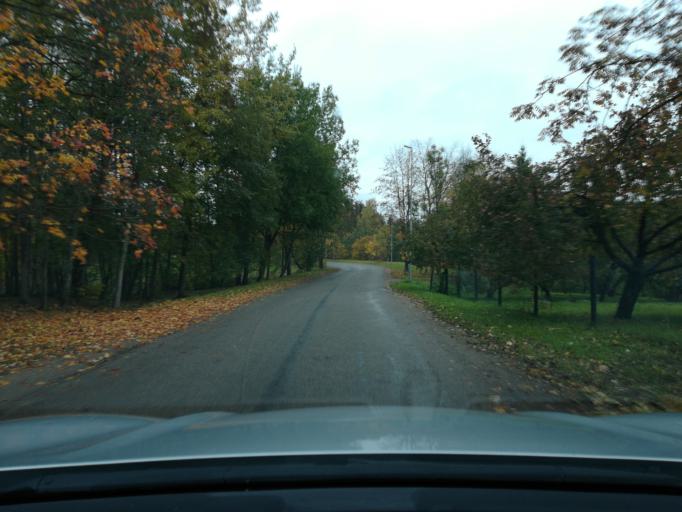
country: EE
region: Ida-Virumaa
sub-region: Johvi vald
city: Johvi
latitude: 59.1970
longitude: 27.5398
